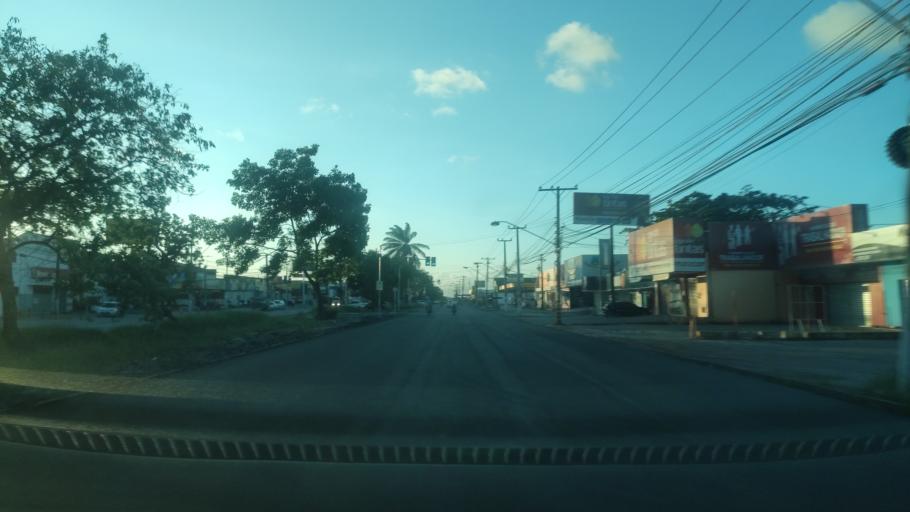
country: BR
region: Alagoas
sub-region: Satuba
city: Satuba
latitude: -9.5769
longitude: -35.7701
